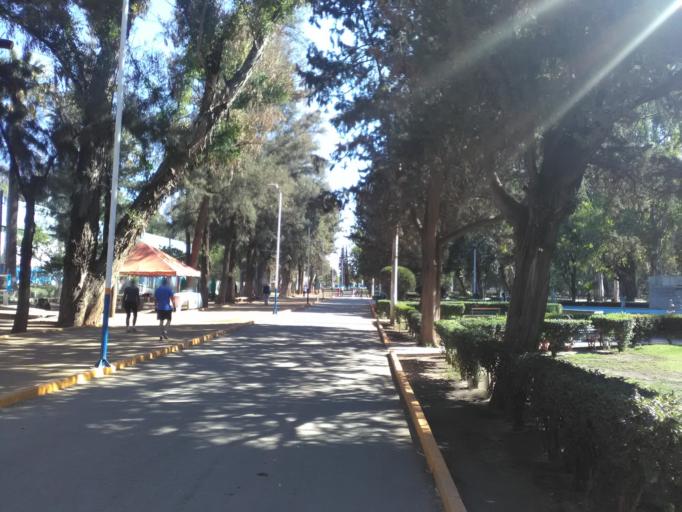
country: MX
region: Durango
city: Victoria de Durango
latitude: 24.0265
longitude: -104.6854
